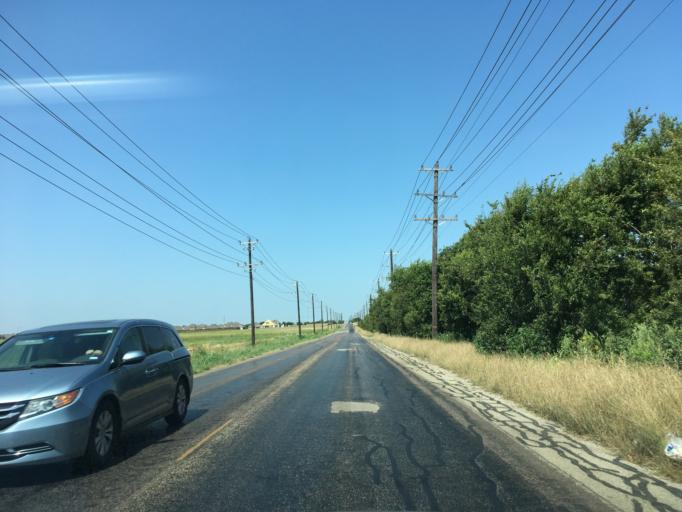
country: US
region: Texas
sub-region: Collin County
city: Prosper
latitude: 33.2038
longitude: -96.7740
